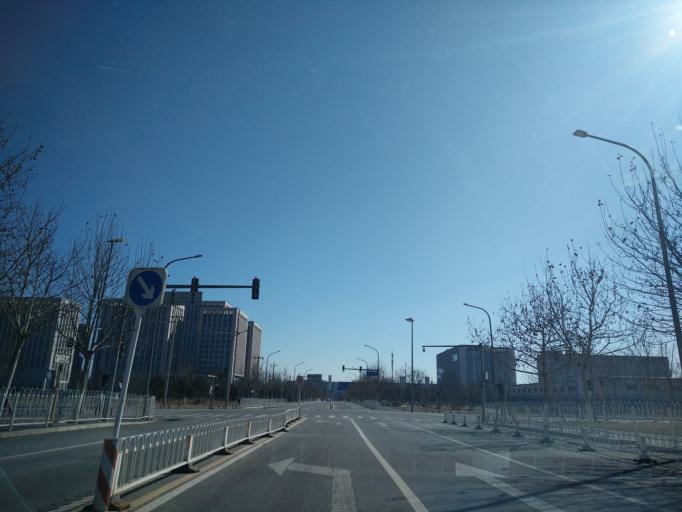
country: CN
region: Beijing
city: Yinghai
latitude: 39.7503
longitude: 116.4927
